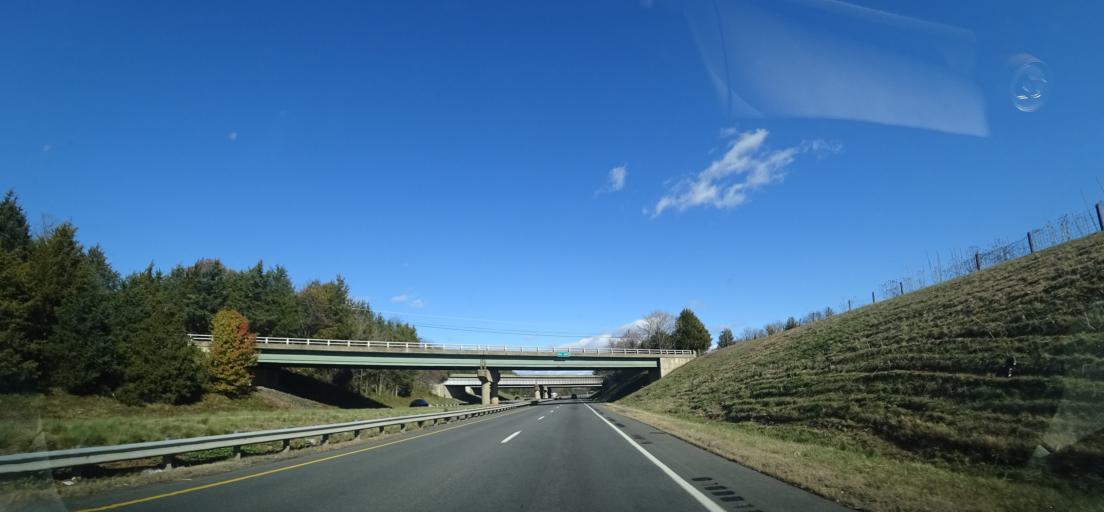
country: US
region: Virginia
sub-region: Culpeper County
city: Culpeper
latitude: 38.4876
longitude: -77.9377
